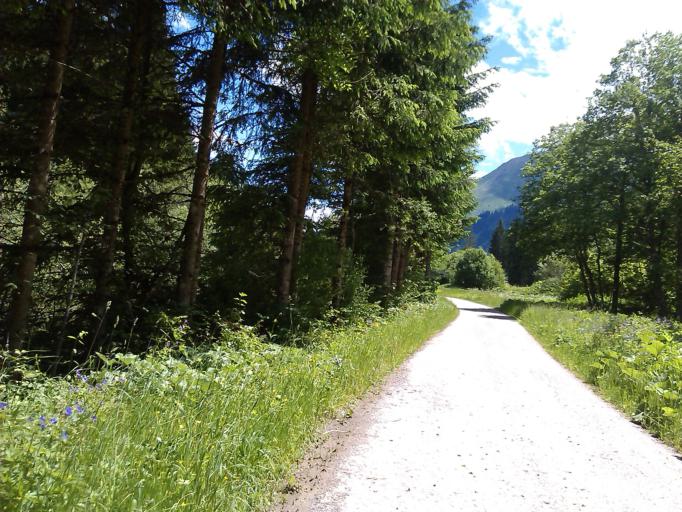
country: AT
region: Tyrol
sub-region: Politischer Bezirk Reutte
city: Bichlbach
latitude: 47.4287
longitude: 10.7733
